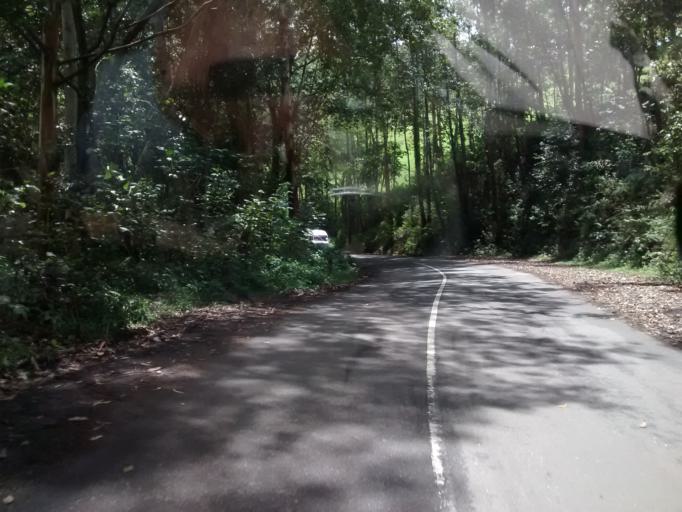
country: IN
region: Kerala
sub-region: Idukki
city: Munnar
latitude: 10.1160
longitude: 77.1381
